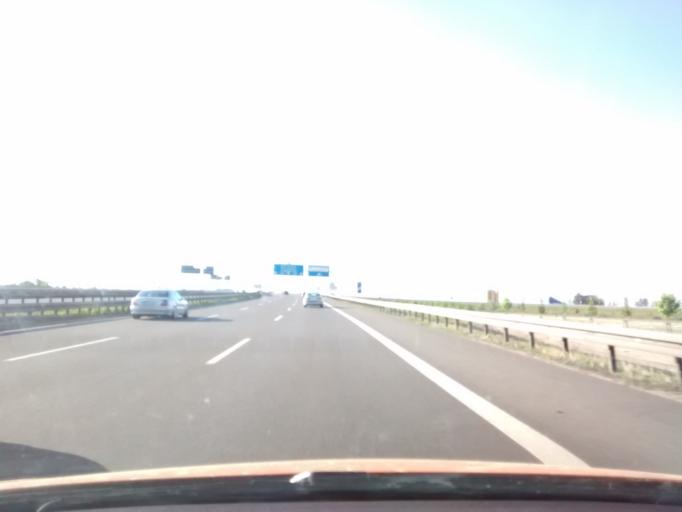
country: DE
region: Brandenburg
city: Schonefeld
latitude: 52.3732
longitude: 13.5468
